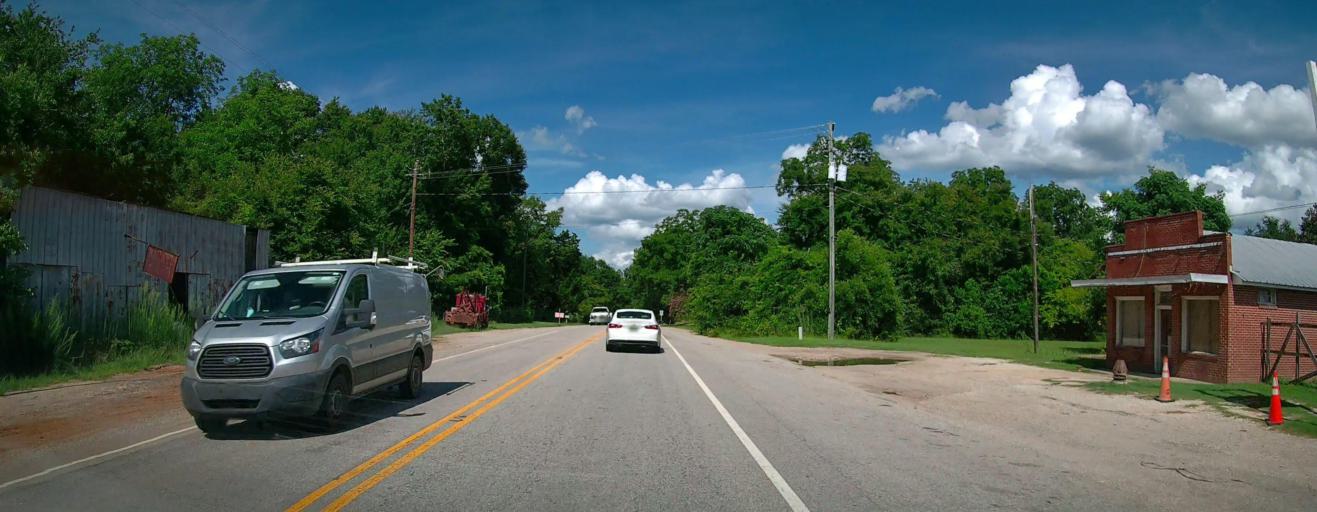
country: US
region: Alabama
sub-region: Lee County
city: Auburn
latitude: 32.4269
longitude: -85.4445
